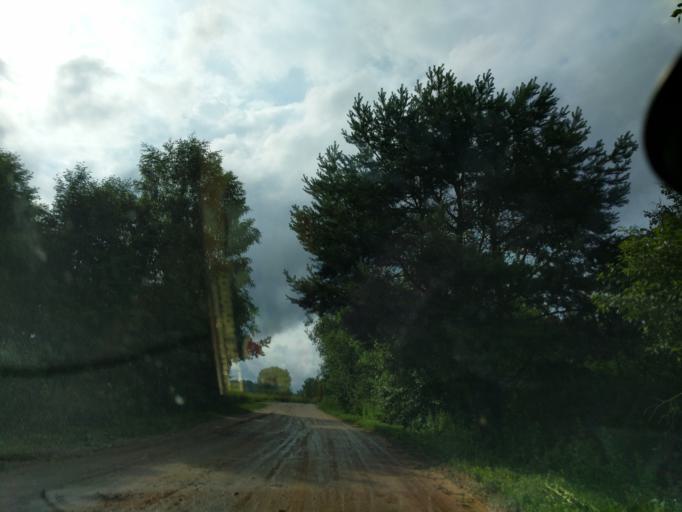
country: RU
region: Kaluga
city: Nikola-Lenivets
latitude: 54.7509
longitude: 35.6313
